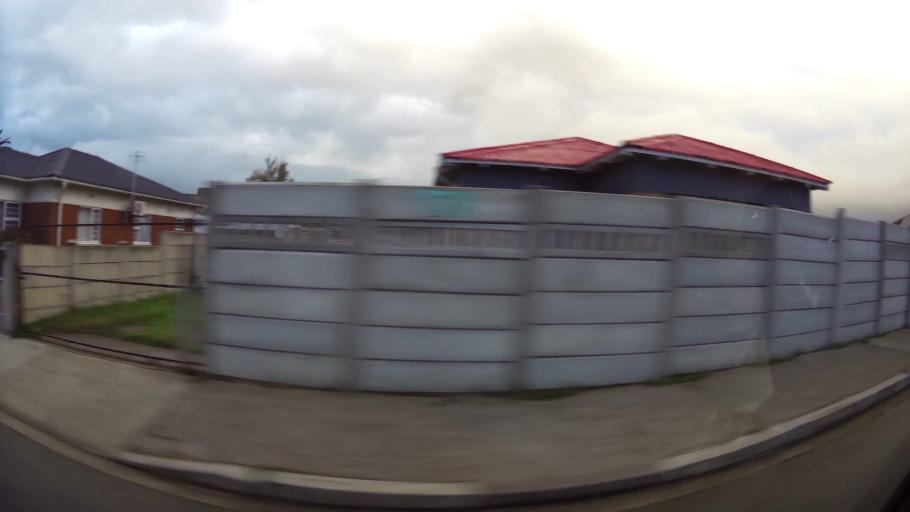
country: ZA
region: Eastern Cape
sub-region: Nelson Mandela Bay Metropolitan Municipality
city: Port Elizabeth
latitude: -33.9263
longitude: 25.6002
